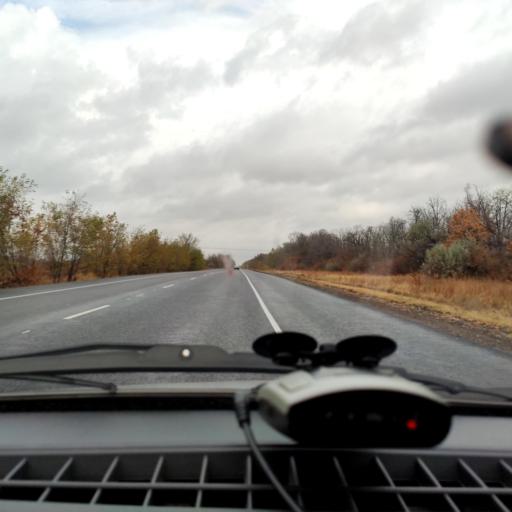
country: RU
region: Voronezj
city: Kolodeznyy
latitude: 51.2378
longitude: 39.0579
